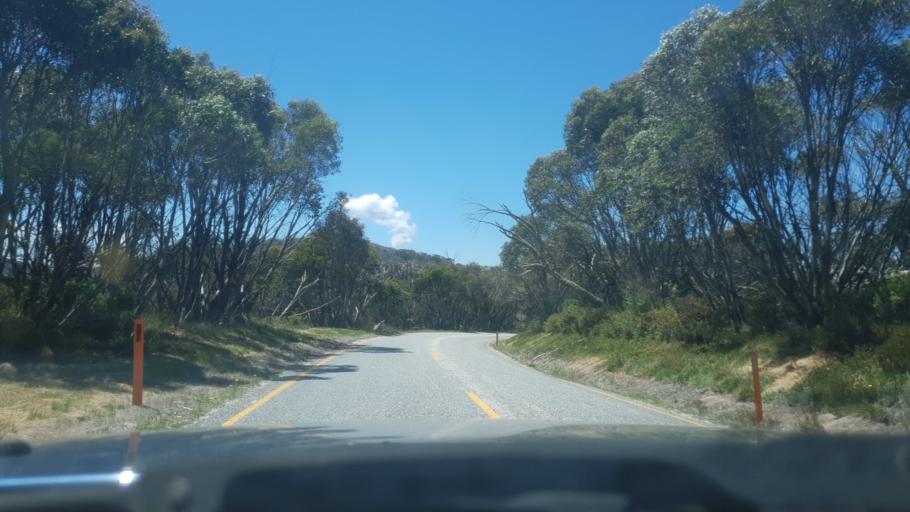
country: AU
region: Victoria
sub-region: Alpine
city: Mount Beauty
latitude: -36.9410
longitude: 147.3164
